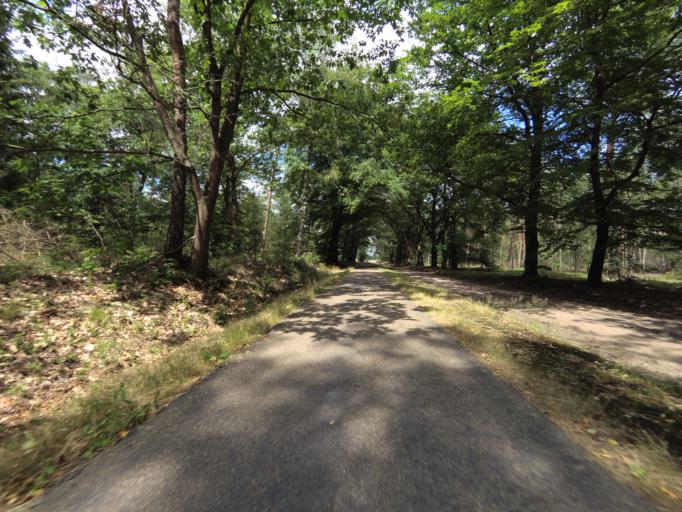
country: NL
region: Overijssel
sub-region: Gemeente Hof van Twente
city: Markelo
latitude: 52.3336
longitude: 6.4503
